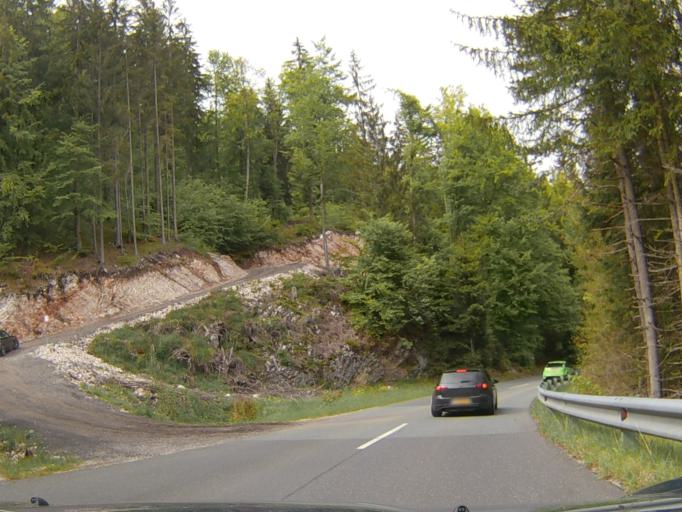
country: AT
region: Carinthia
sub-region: Villach Stadt
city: Villach
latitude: 46.5982
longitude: 13.8033
